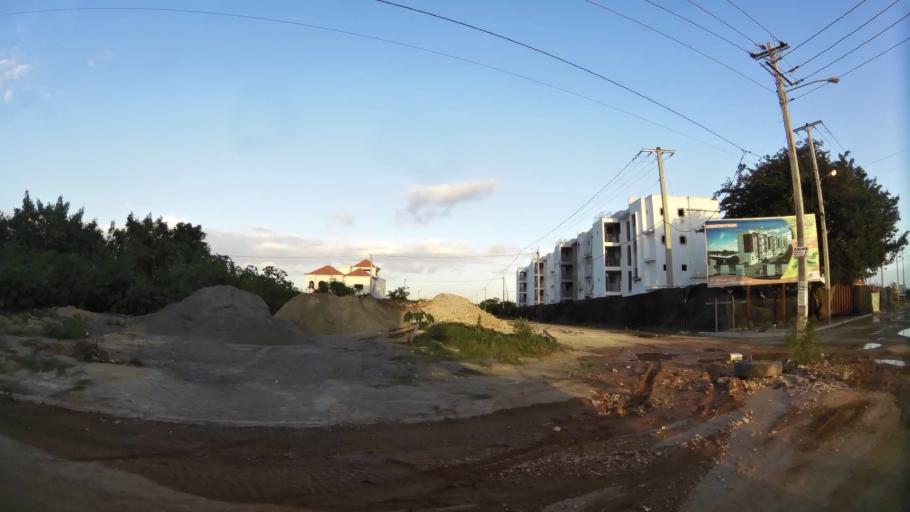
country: DO
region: Santo Domingo
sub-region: Santo Domingo
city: Santo Domingo Este
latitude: 18.4873
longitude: -69.8156
